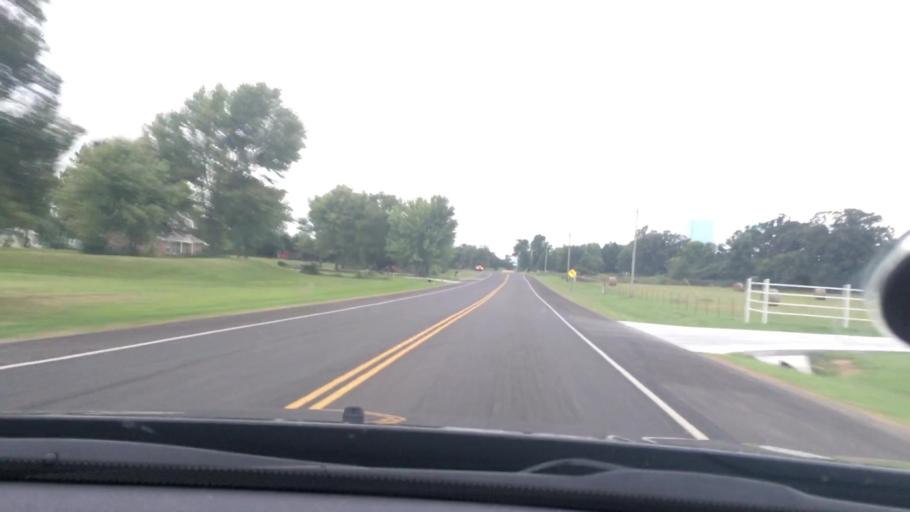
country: US
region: Oklahoma
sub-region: Sequoyah County
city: Vian
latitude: 35.5699
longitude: -94.9853
